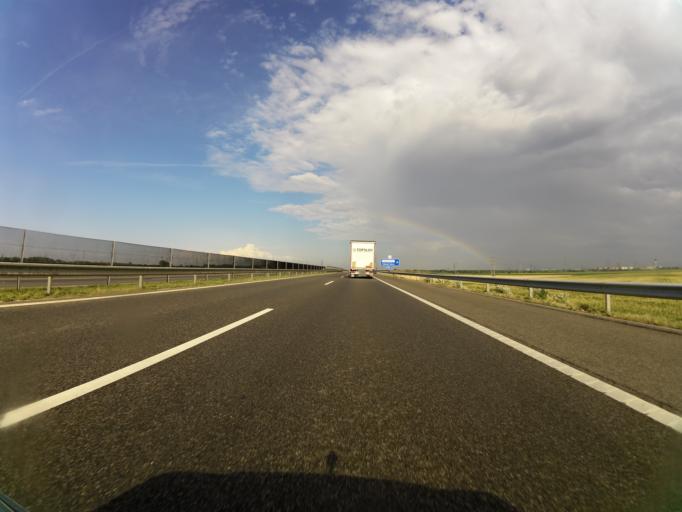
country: HU
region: Csongrad
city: Szeged
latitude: 46.2950
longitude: 20.1219
